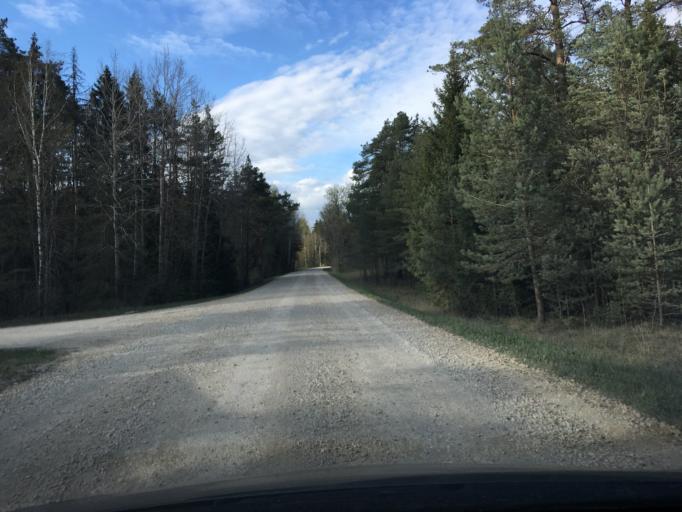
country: EE
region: Raplamaa
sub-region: Maerjamaa vald
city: Marjamaa
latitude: 58.9674
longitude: 24.3317
